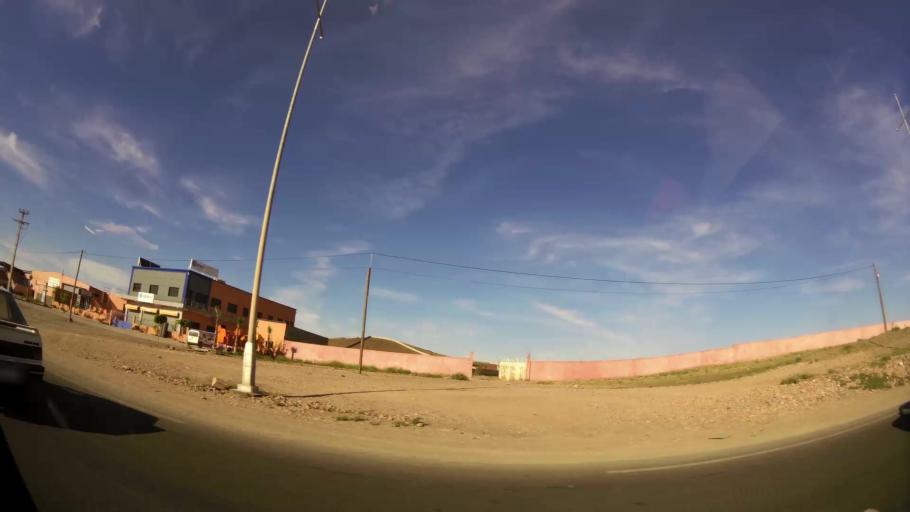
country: MA
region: Marrakech-Tensift-Al Haouz
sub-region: Marrakech
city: Marrakesh
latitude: 31.7082
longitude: -8.0651
